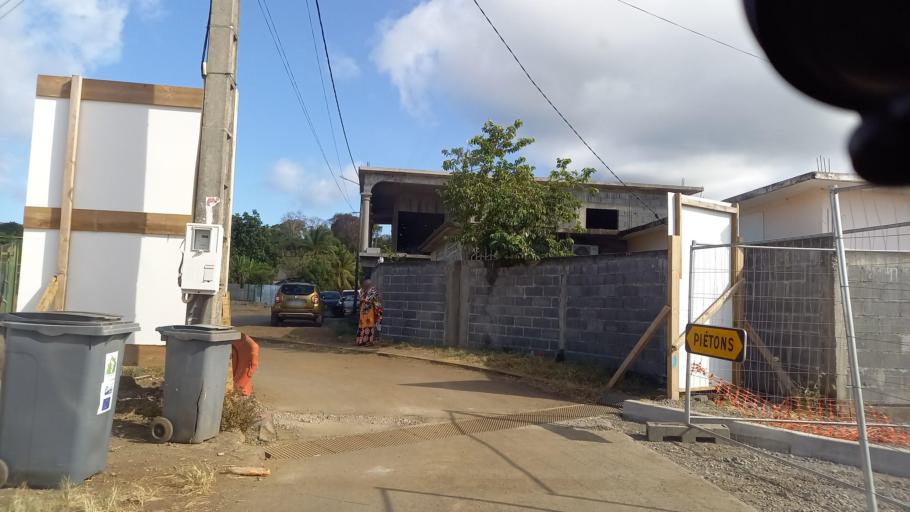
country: YT
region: Bandrele
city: Bandrele
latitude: -12.9089
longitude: 45.1960
